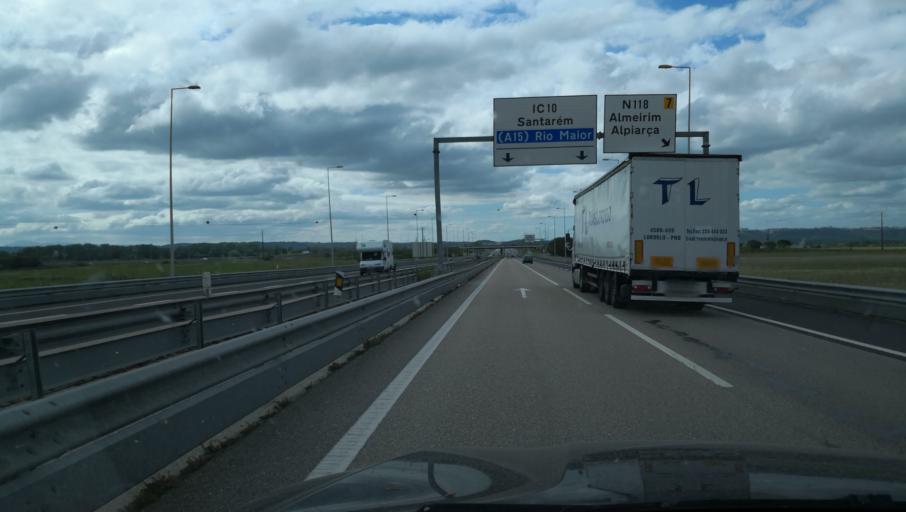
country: PT
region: Santarem
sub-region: Almeirim
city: Almeirim
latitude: 39.1878
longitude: -8.6437
